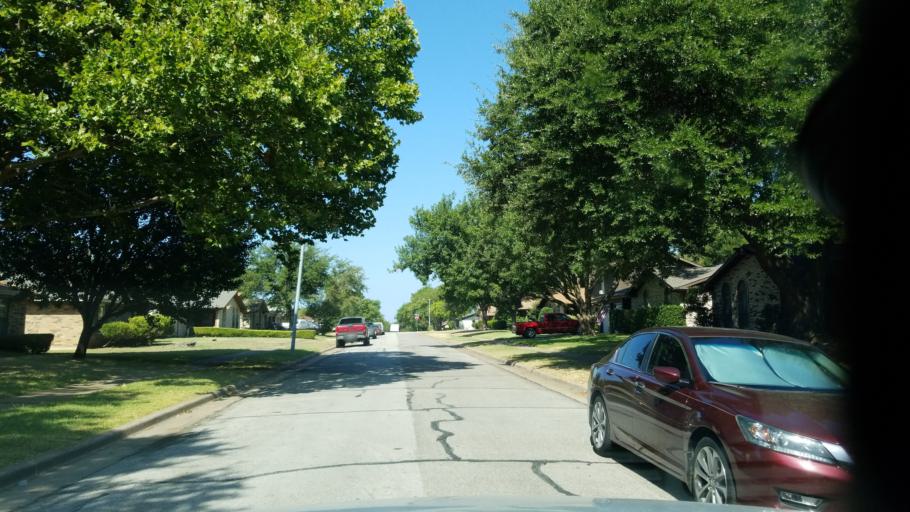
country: US
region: Texas
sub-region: Dallas County
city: Duncanville
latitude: 32.6355
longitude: -96.9015
